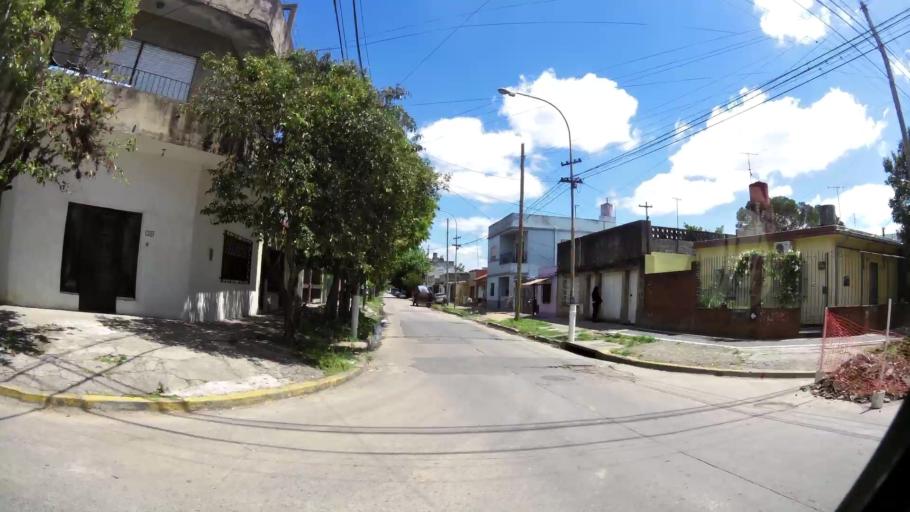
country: AR
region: Buenos Aires
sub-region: Partido de Lanus
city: Lanus
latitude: -34.7236
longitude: -58.4122
